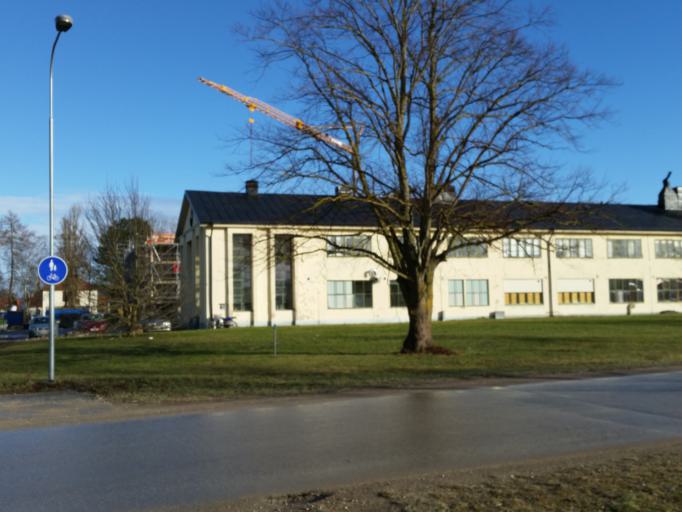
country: SE
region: Gotland
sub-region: Gotland
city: Visby
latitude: 57.6313
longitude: 18.3033
